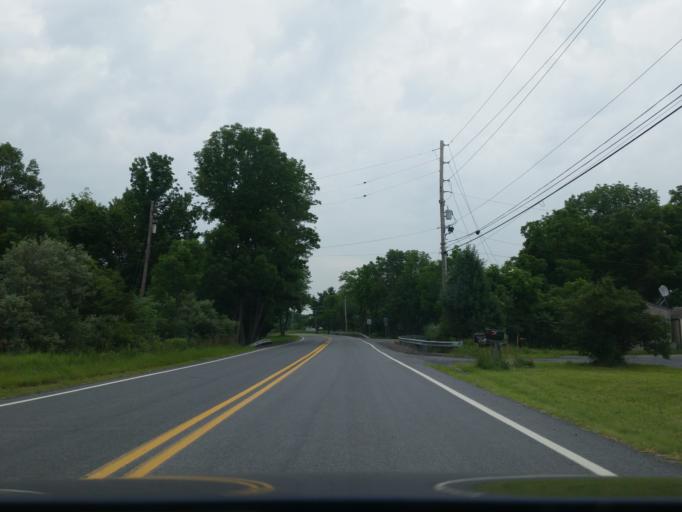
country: US
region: Pennsylvania
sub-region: Dauphin County
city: Skyline View
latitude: 40.4010
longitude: -76.6557
